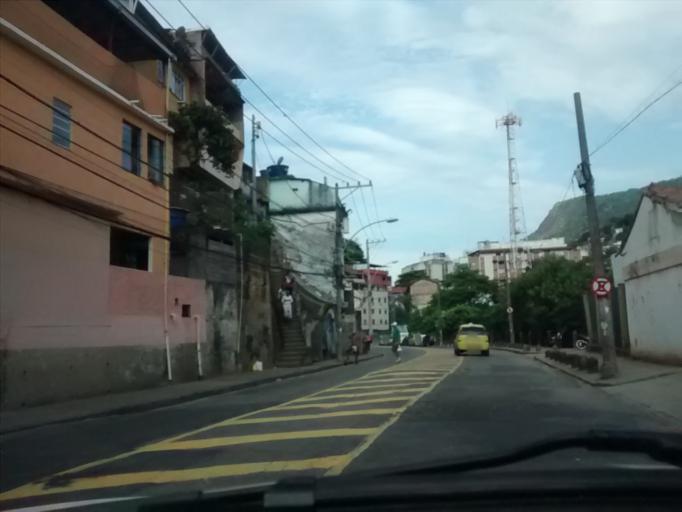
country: BR
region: Rio de Janeiro
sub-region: Rio De Janeiro
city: Rio de Janeiro
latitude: -22.9399
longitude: -43.2532
